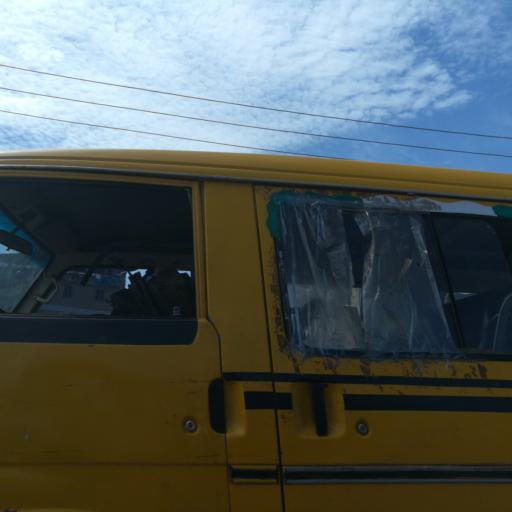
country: NG
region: Lagos
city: Lagos
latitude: 6.4651
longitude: 3.3874
